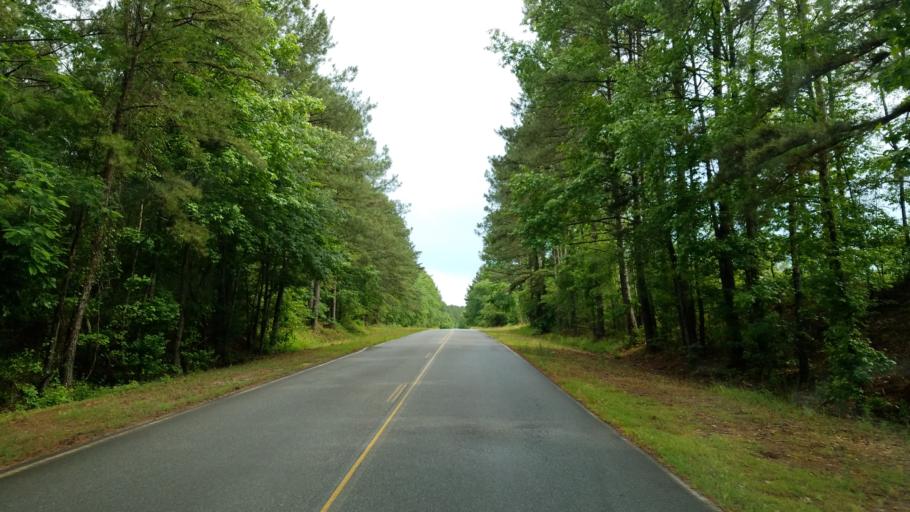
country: US
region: Georgia
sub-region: Dooly County
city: Unadilla
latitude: 32.3178
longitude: -83.7898
